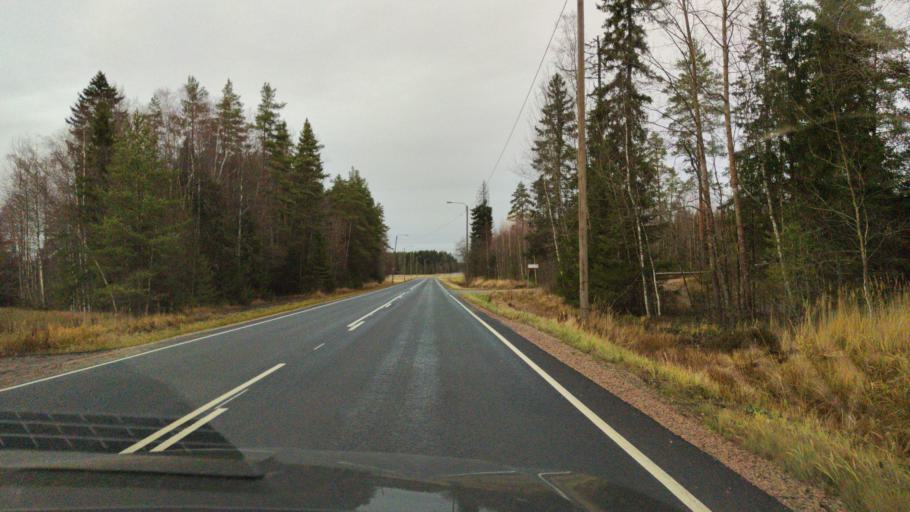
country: FI
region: Varsinais-Suomi
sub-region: Turku
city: Vahto
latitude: 60.6630
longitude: 22.4345
